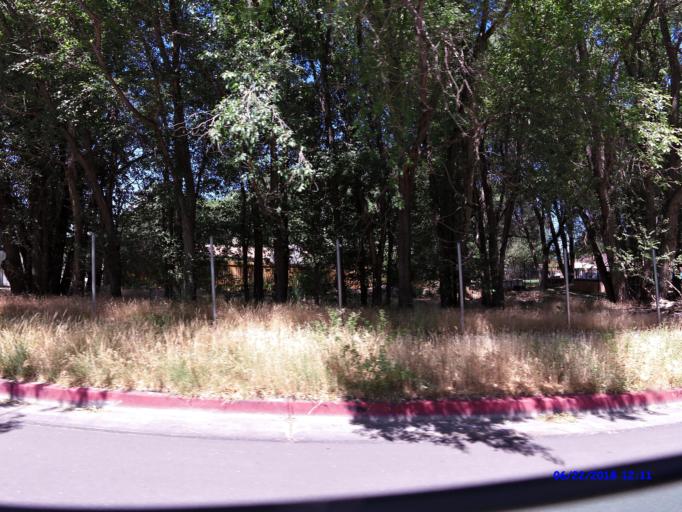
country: US
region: Utah
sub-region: Weber County
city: Ogden
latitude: 41.2374
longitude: -111.9530
